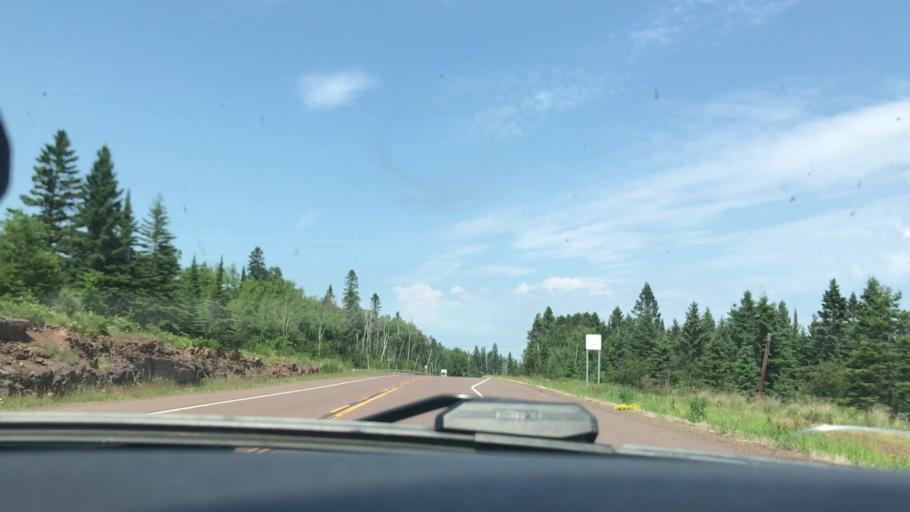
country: US
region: Minnesota
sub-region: Cook County
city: Grand Marais
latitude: 47.6172
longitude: -90.7550
